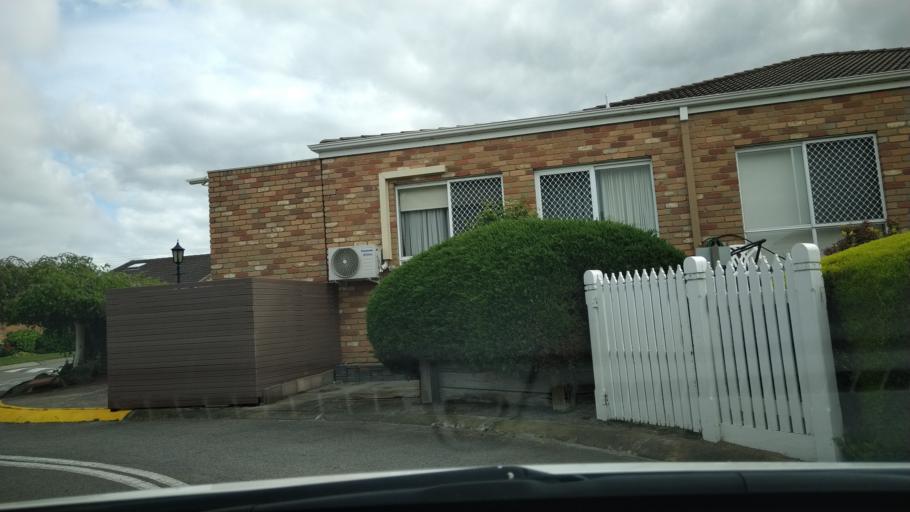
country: AU
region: Victoria
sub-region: Greater Dandenong
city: Keysborough
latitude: -37.9945
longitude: 145.1647
